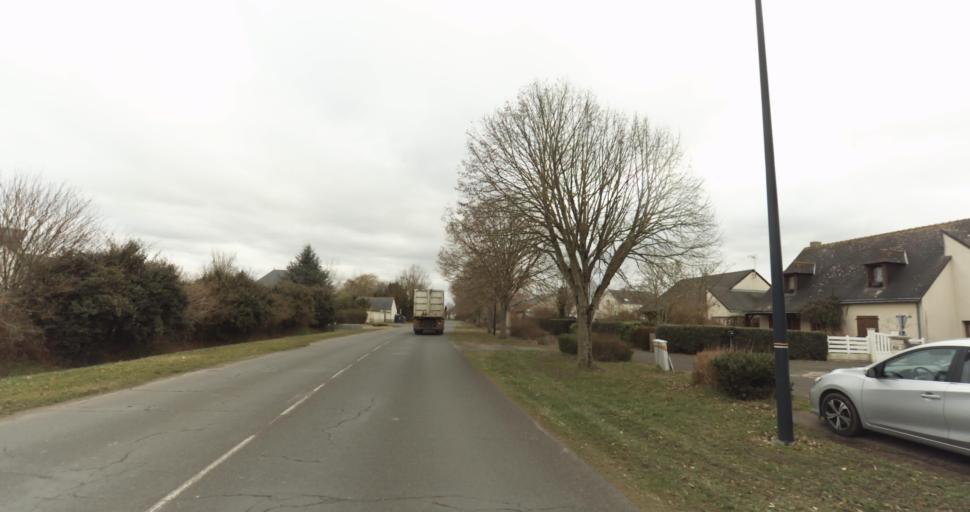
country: FR
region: Pays de la Loire
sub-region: Departement de Maine-et-Loire
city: Saumur
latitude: 47.2753
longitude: -0.0728
